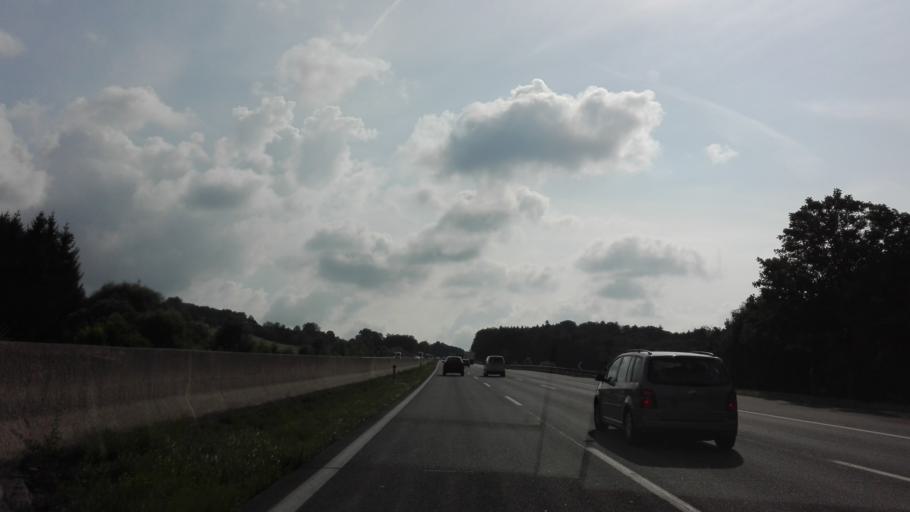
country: AT
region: Lower Austria
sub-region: Politischer Bezirk Amstetten
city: Sankt Georgen am Ybbsfelde
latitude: 48.1382
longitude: 14.9375
